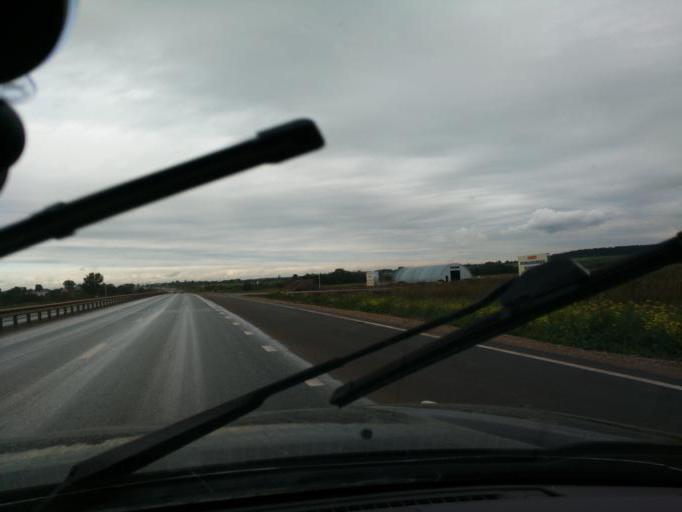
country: RU
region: Perm
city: Kultayevo
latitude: 57.9017
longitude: 55.9766
